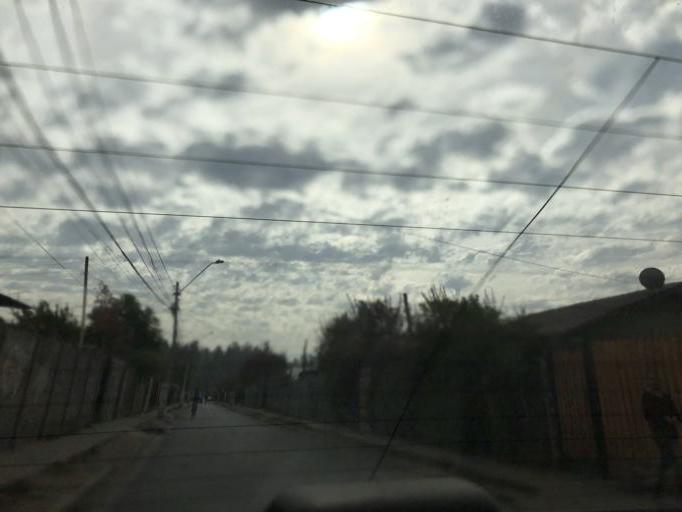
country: CL
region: Santiago Metropolitan
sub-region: Provincia de Cordillera
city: Puente Alto
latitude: -33.6091
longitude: -70.5216
